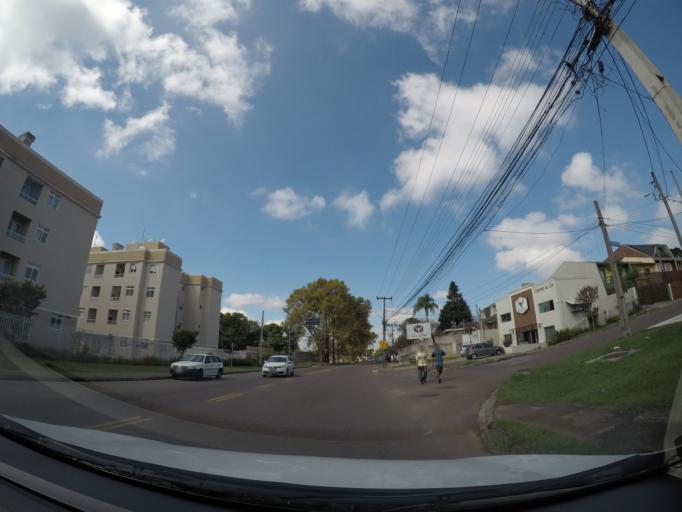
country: BR
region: Parana
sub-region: Sao Jose Dos Pinhais
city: Sao Jose dos Pinhais
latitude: -25.4899
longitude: -49.2227
